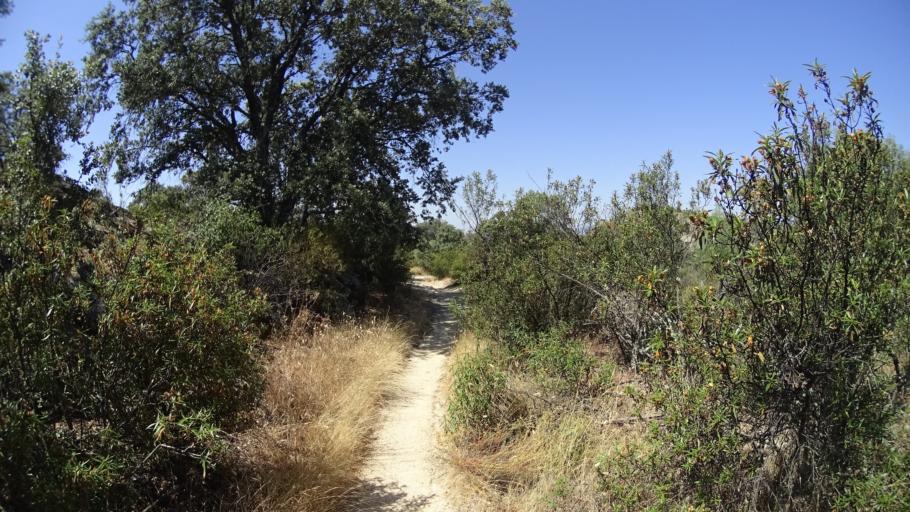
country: ES
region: Madrid
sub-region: Provincia de Madrid
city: Moralzarzal
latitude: 40.6349
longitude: -3.9535
